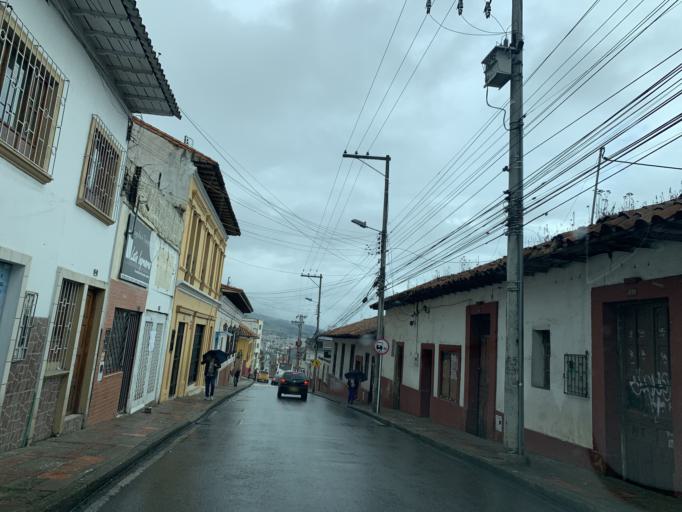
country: CO
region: Boyaca
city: Tunja
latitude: 5.5318
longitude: -73.3601
